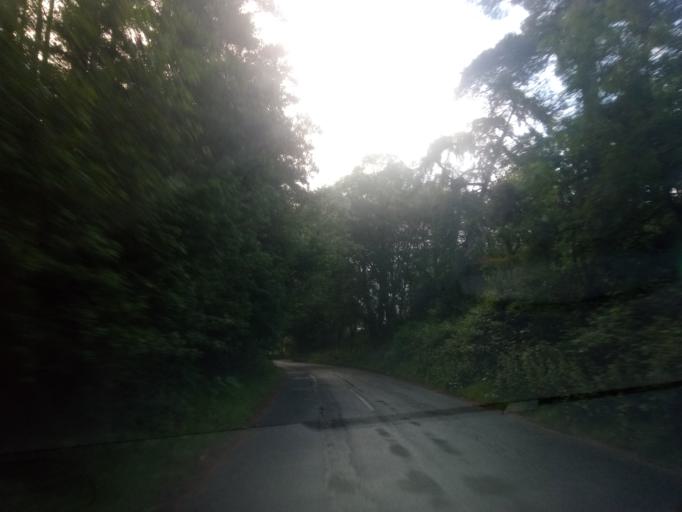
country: GB
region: England
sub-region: Northumberland
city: Bardon Mill
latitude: 54.8829
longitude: -2.2488
